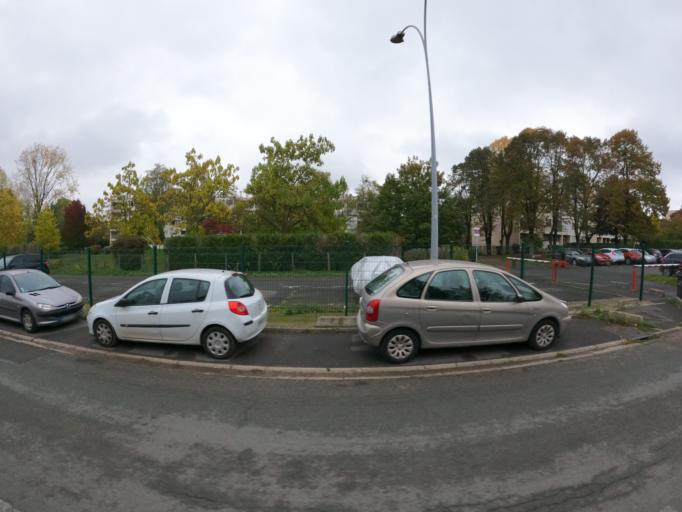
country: FR
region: Ile-de-France
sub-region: Departement du Val-de-Marne
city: Chennevieres-sur-Marne
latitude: 48.7890
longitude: 2.5281
